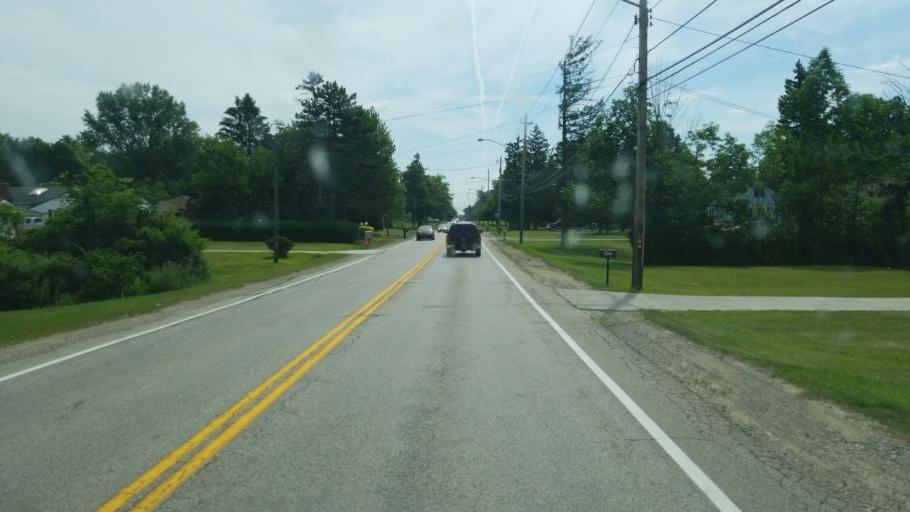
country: US
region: Ohio
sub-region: Cuyahoga County
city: North Royalton
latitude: 41.3138
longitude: -81.7153
